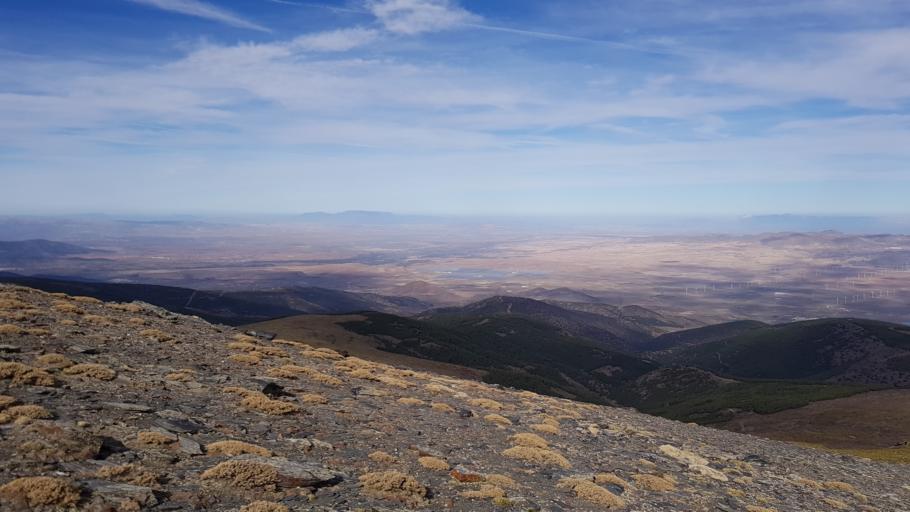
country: ES
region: Andalusia
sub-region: Provincia de Almeria
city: Bayarcal
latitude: 37.0950
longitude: -2.9996
